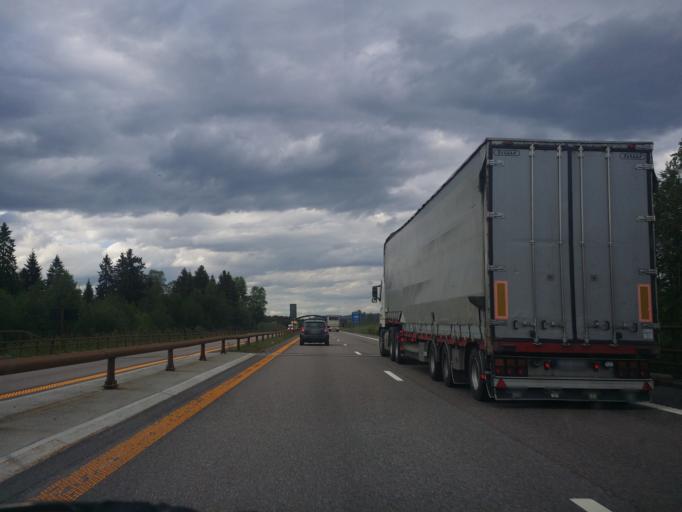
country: NO
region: Akershus
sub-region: Eidsvoll
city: Eidsvoll
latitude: 60.3768
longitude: 11.2078
